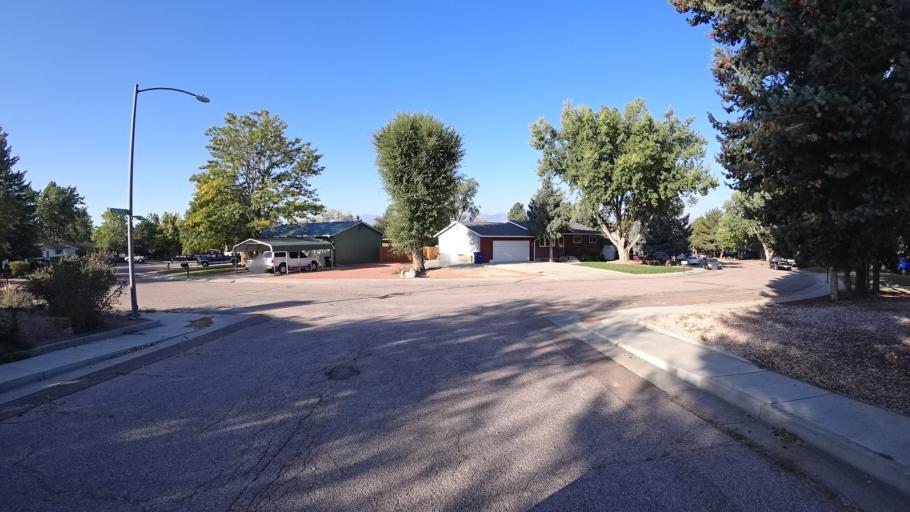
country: US
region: Colorado
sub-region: El Paso County
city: Cimarron Hills
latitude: 38.8891
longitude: -104.7514
